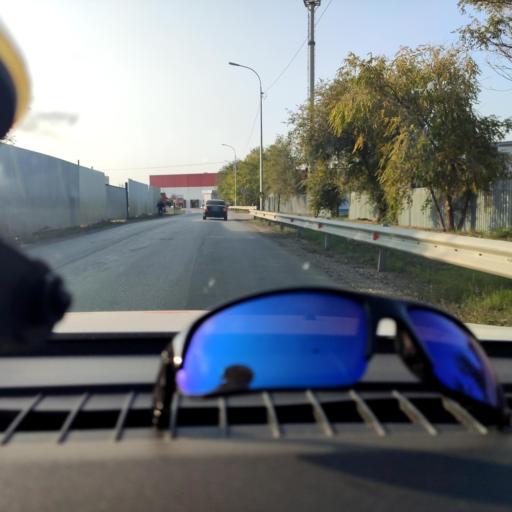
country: RU
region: Samara
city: Samara
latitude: 53.0973
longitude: 50.1379
